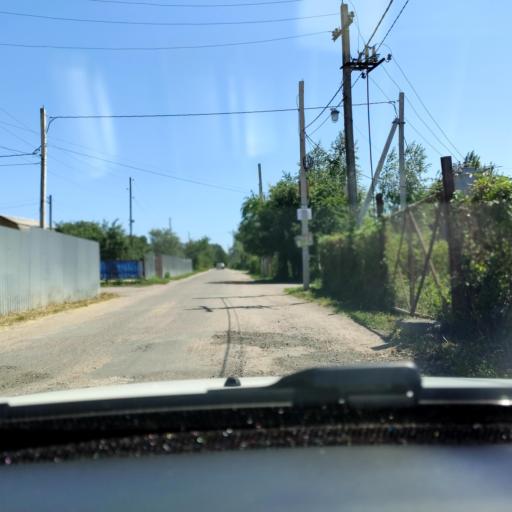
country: RU
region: Voronezj
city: Shilovo
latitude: 51.5870
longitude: 39.1561
